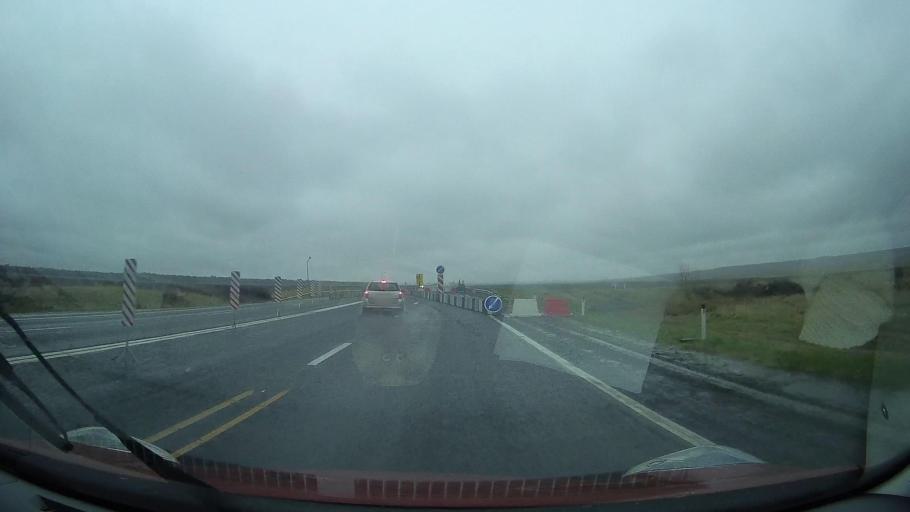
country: RU
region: Stavropol'skiy
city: Nevinnomyssk
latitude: 44.6257
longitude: 42.0578
